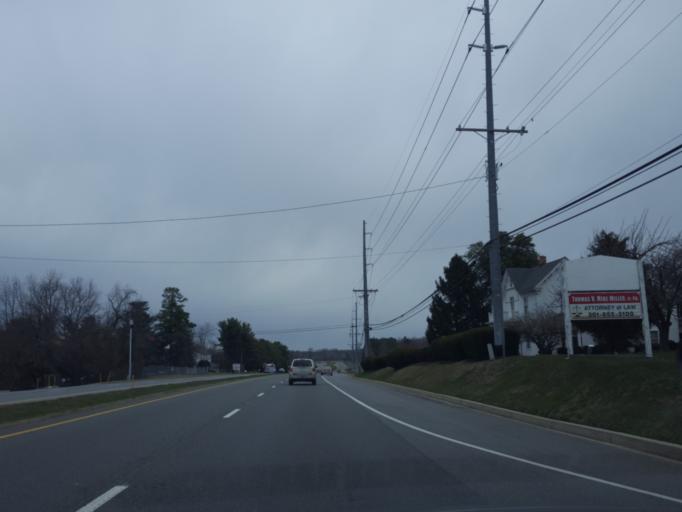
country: US
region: Maryland
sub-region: Calvert County
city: Dunkirk
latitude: 38.7216
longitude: -76.6605
